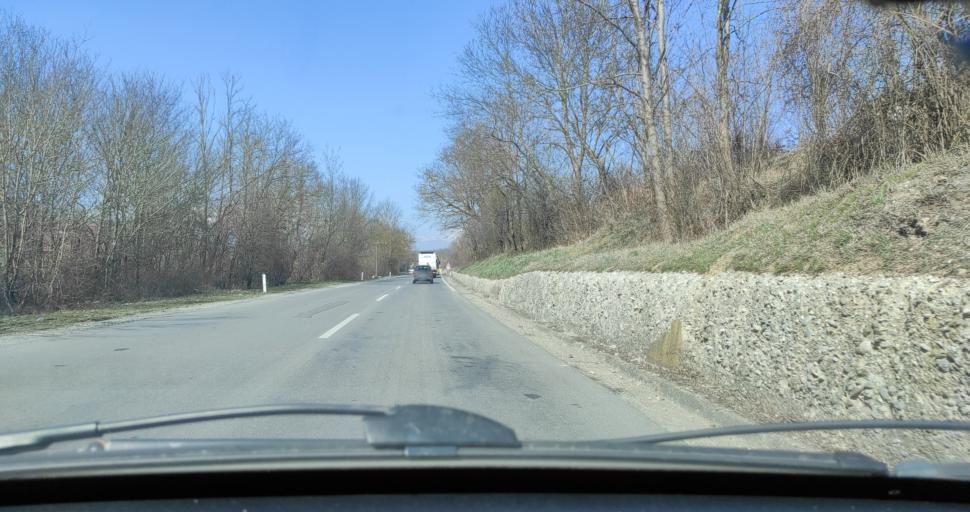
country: XK
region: Pec
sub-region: Komuna e Pejes
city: Kosuriq
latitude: 42.6317
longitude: 20.4505
